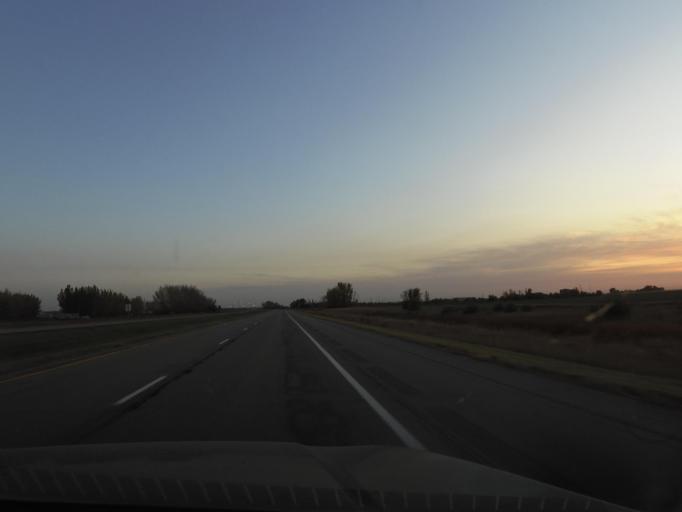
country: US
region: North Dakota
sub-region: Walsh County
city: Grafton
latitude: 48.5815
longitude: -97.1831
